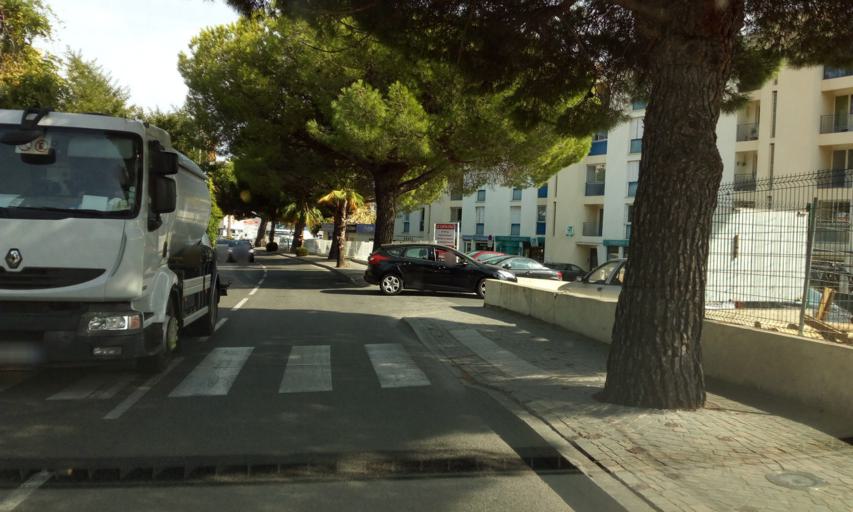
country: FR
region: Provence-Alpes-Cote d'Azur
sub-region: Departement du Var
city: Le Lavandou
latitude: 43.1381
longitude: 6.3615
